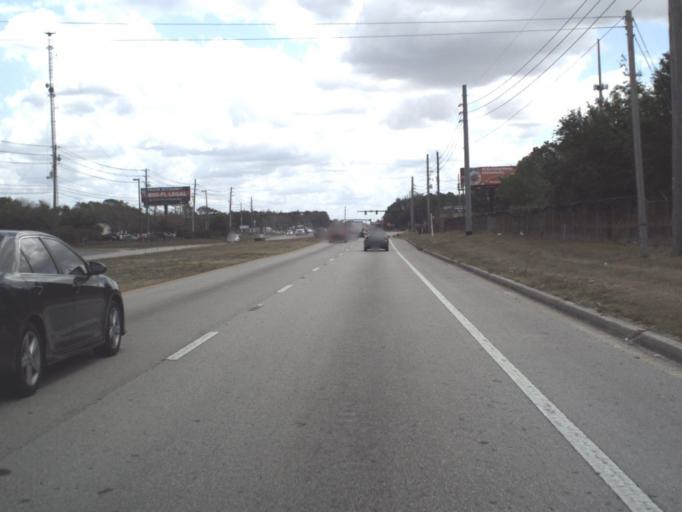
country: US
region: Florida
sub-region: Orange County
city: Tangelo Park
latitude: 28.4499
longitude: -81.4450
